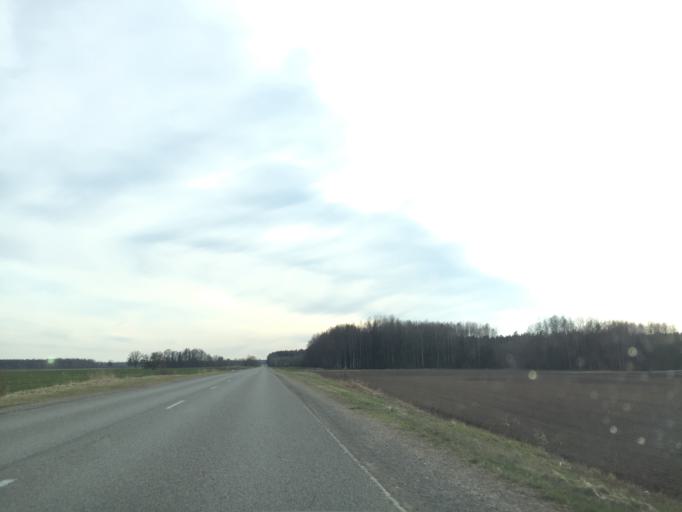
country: LV
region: Lielvarde
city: Lielvarde
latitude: 56.7889
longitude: 24.8036
